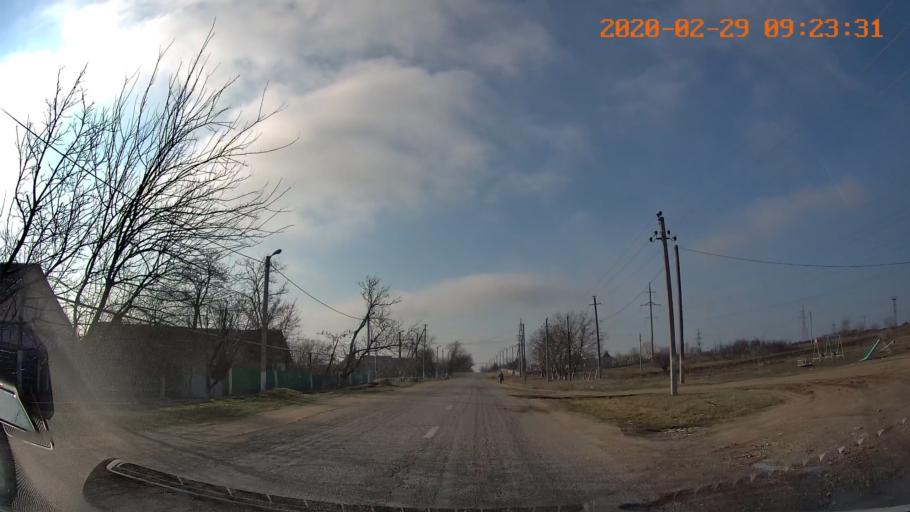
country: MD
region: Telenesti
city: Pervomaisc
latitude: 46.7250
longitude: 29.9610
